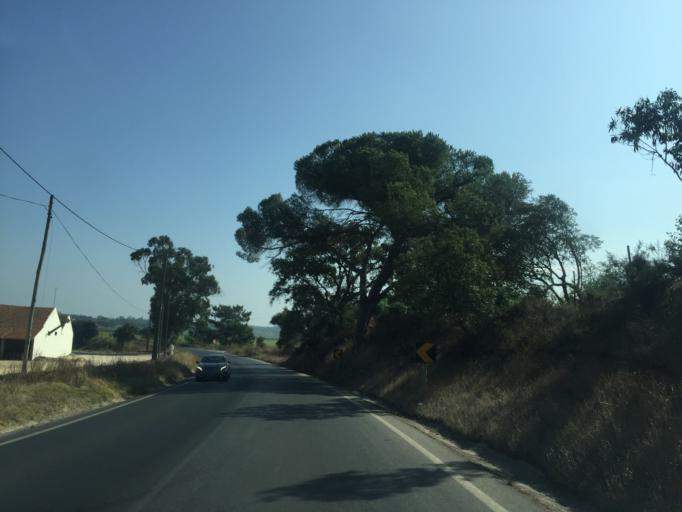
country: PT
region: Santarem
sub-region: Salvaterra de Magos
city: Marinhais
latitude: 39.0304
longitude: -8.7443
